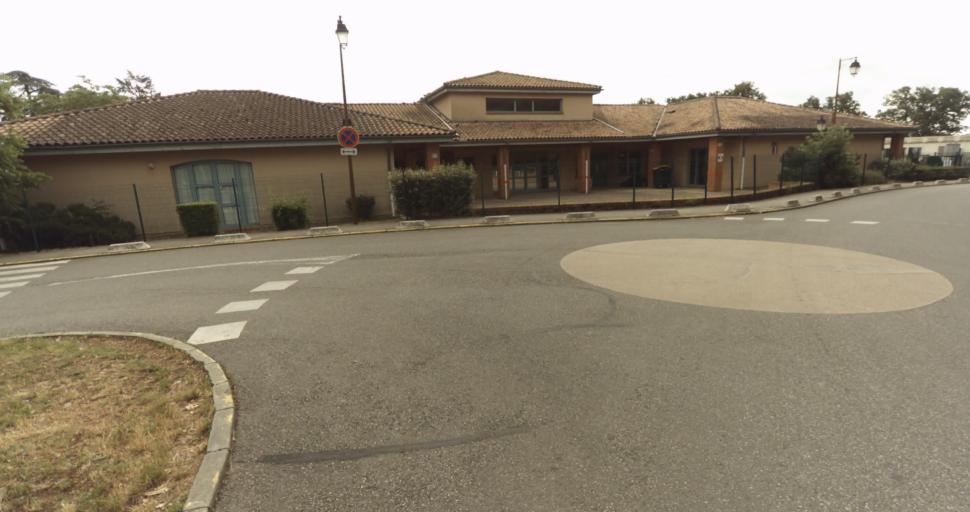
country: FR
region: Midi-Pyrenees
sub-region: Departement de la Haute-Garonne
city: Fonsorbes
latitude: 43.5515
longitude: 1.2339
